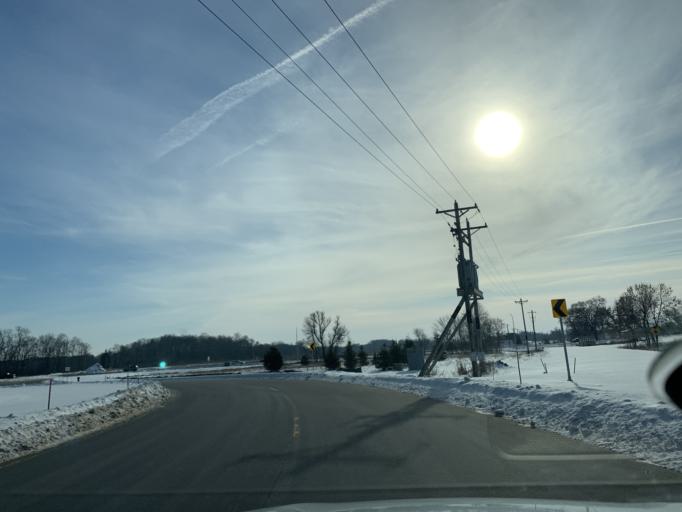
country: US
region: Minnesota
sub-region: Anoka County
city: Columbus
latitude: 45.2524
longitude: -93.0216
